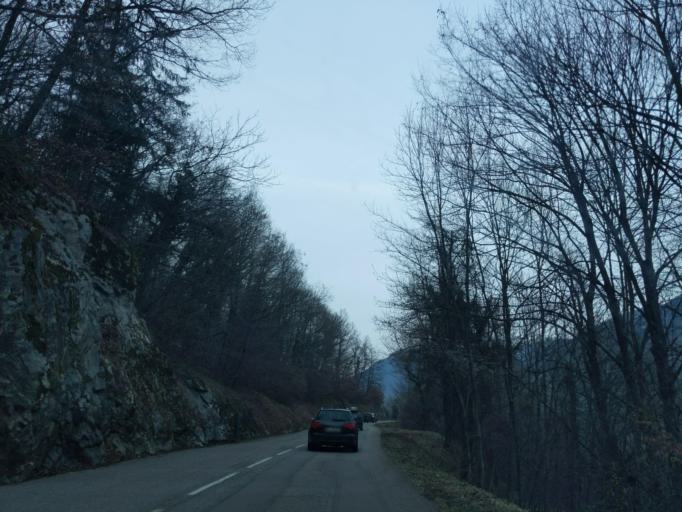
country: FR
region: Rhone-Alpes
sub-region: Departement de la Savoie
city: La Bathie
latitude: 45.6072
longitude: 6.4390
